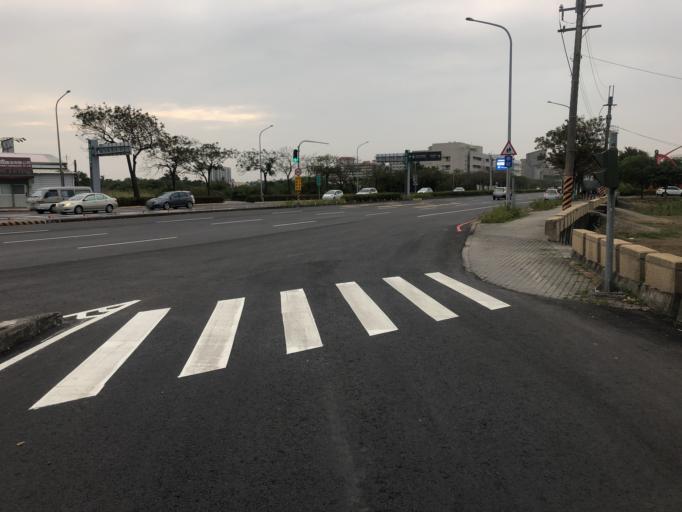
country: TW
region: Taiwan
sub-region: Tainan
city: Tainan
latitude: 23.1065
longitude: 120.2947
